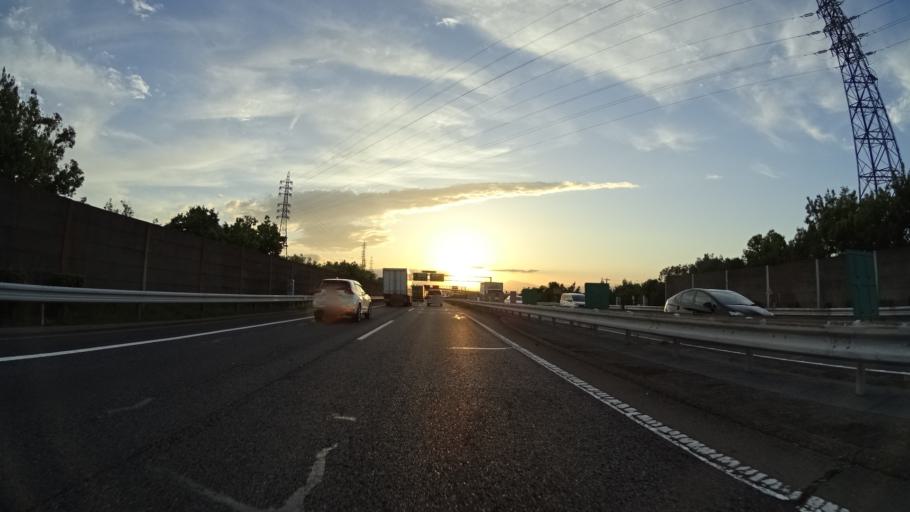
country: JP
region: Aichi
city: Ichinomiya
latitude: 35.2795
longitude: 136.7978
